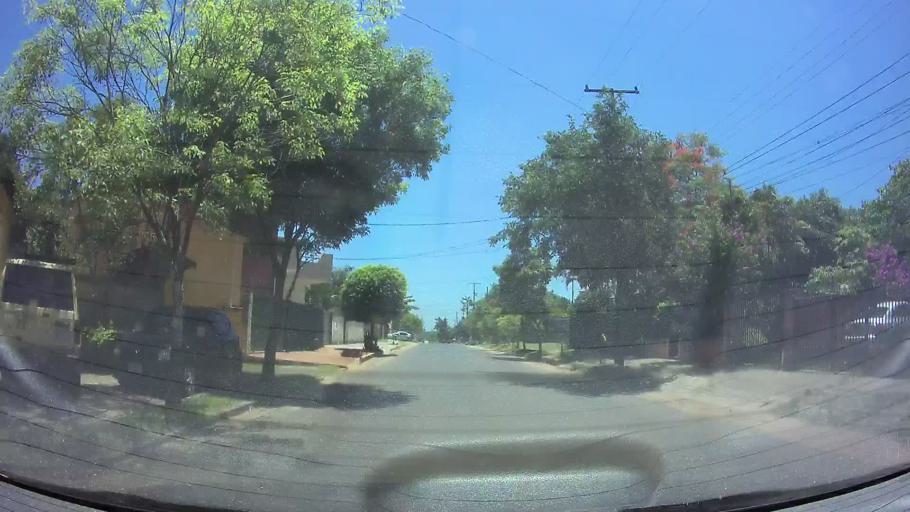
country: PY
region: Central
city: Fernando de la Mora
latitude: -25.2829
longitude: -57.5352
